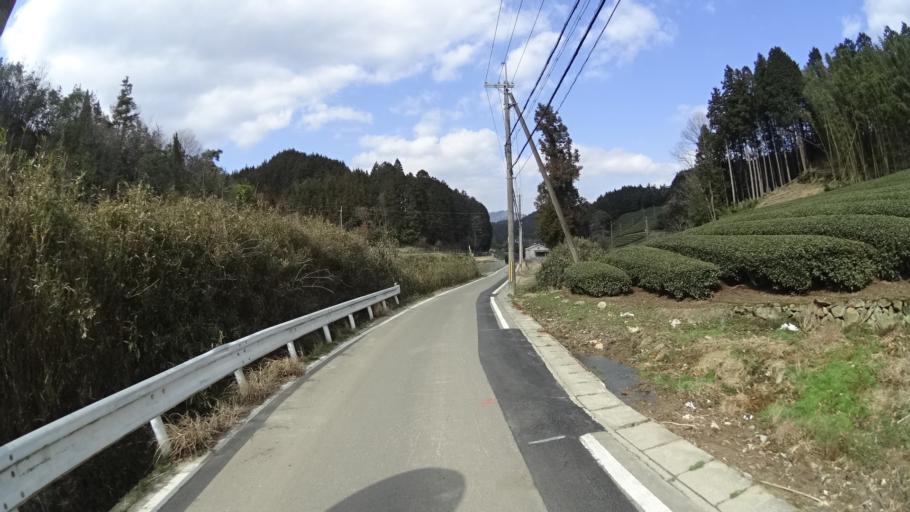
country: JP
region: Nara
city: Nara-shi
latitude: 34.7790
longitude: 135.9075
